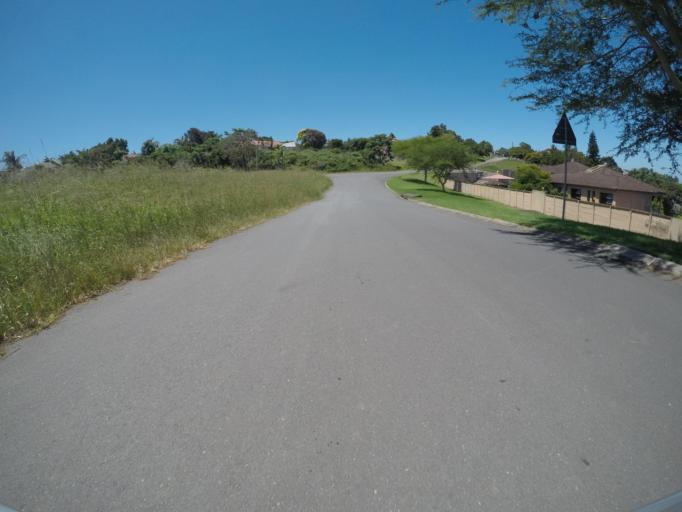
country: ZA
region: Eastern Cape
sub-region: Buffalo City Metropolitan Municipality
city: East London
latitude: -32.9599
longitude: 27.9369
